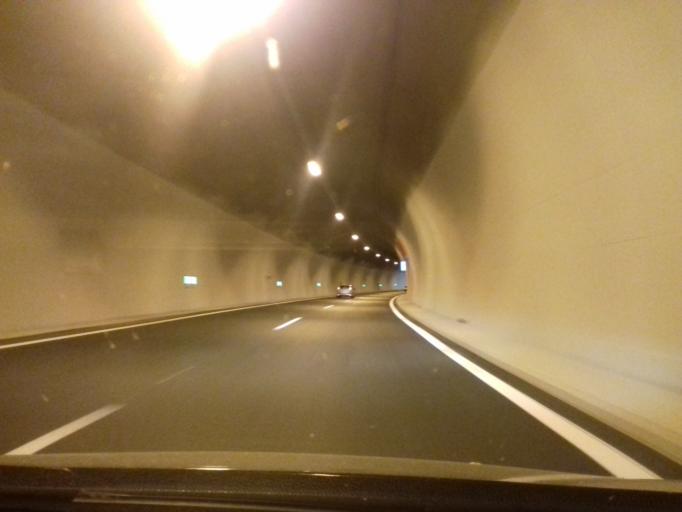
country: GR
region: West Greece
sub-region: Nomos Achaias
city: Akrata
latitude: 38.1678
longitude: 22.2699
